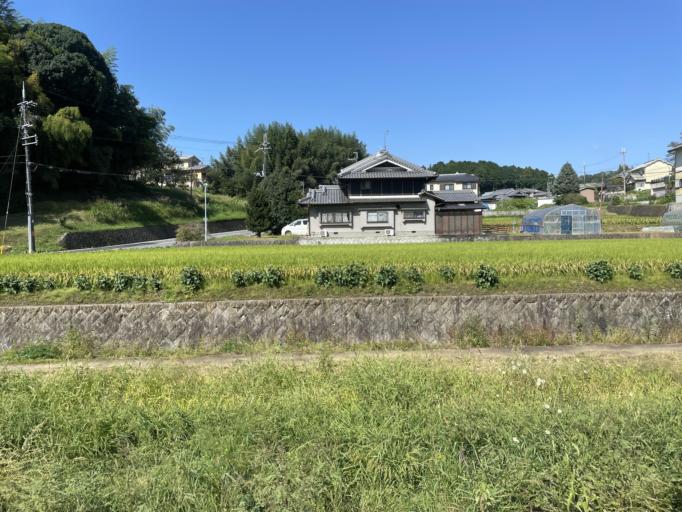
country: JP
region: Nara
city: Kashihara-shi
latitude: 34.4629
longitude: 135.7972
